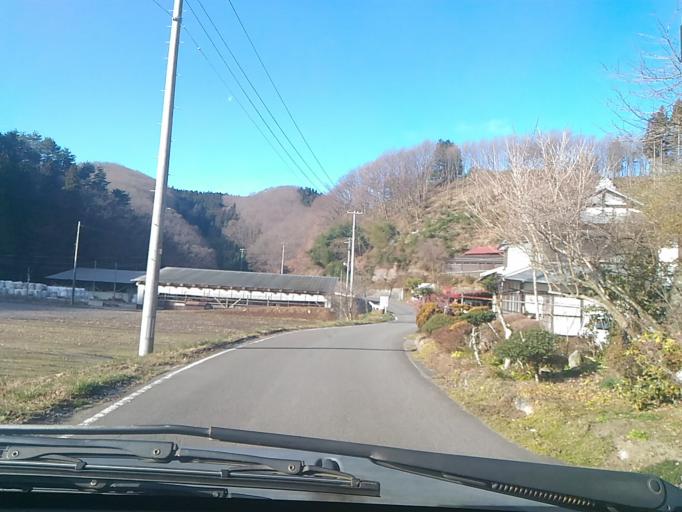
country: JP
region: Fukushima
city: Ishikawa
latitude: 37.0105
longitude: 140.5375
